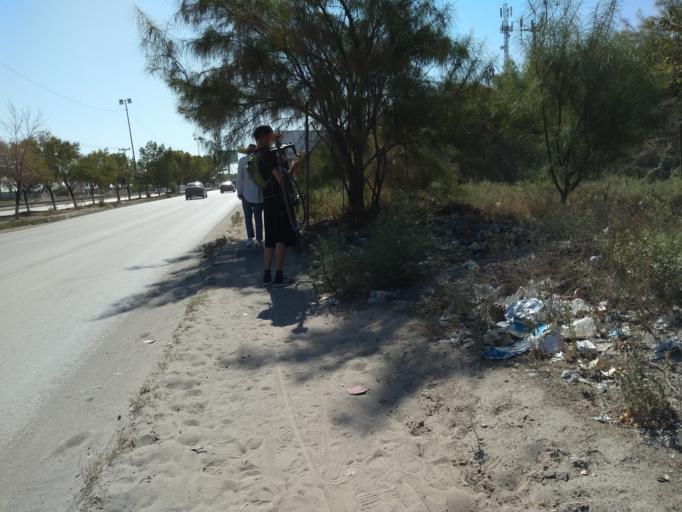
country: US
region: Texas
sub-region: El Paso County
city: El Paso
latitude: 31.7569
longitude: -106.5027
